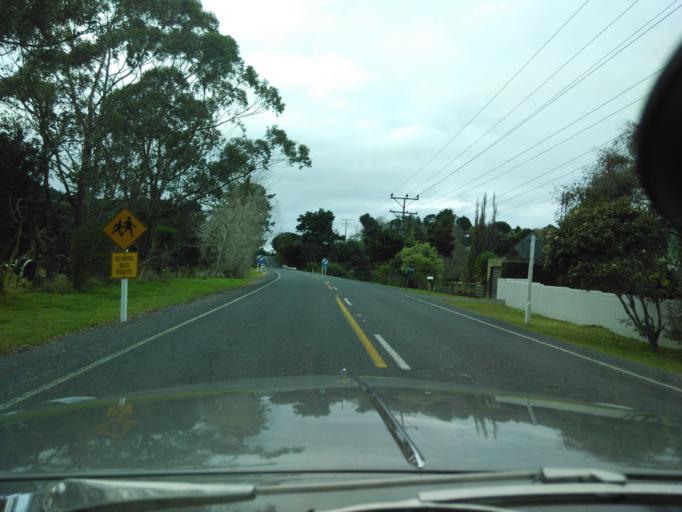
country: NZ
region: Auckland
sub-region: Auckland
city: Parakai
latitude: -36.6337
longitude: 174.5521
